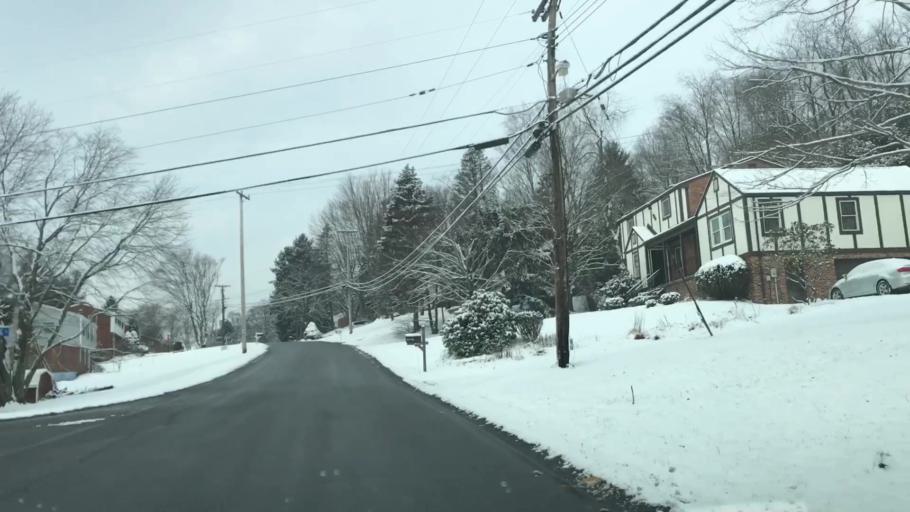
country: US
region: Pennsylvania
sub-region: Allegheny County
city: Allison Park
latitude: 40.5702
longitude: -79.9689
